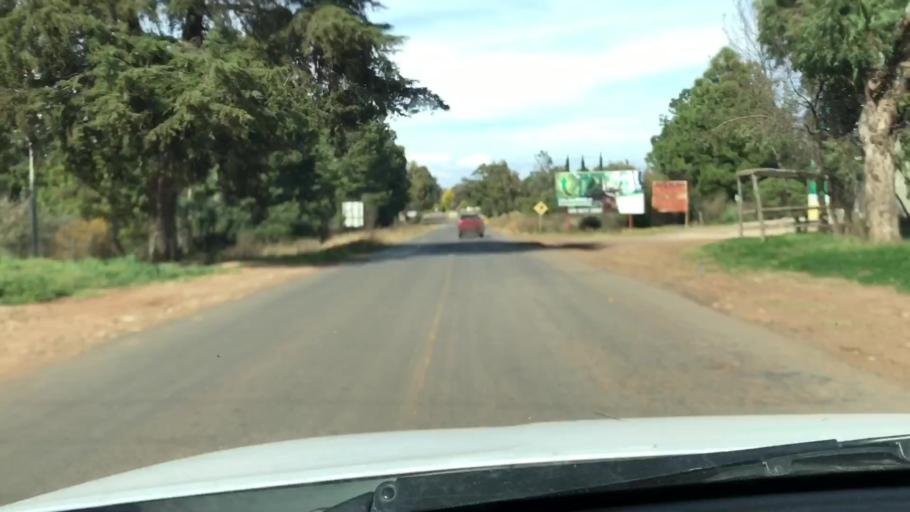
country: MX
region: Jalisco
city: Chiquilistlan
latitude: 20.1240
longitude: -103.7239
